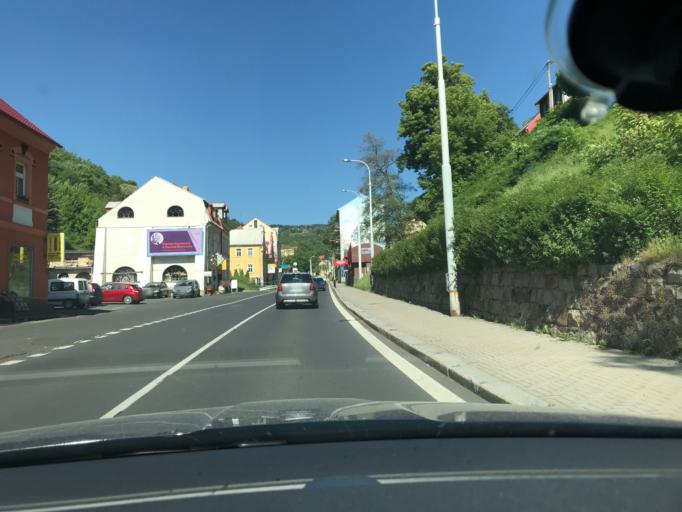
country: CZ
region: Karlovarsky
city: Jachymov
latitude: 50.3621
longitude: 12.9300
